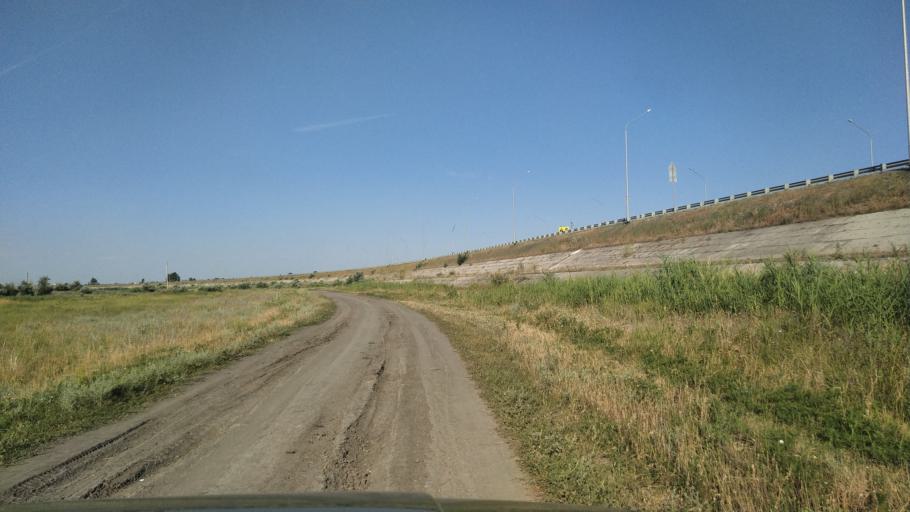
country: RU
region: Rostov
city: Bataysk
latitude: 47.1192
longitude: 39.6535
